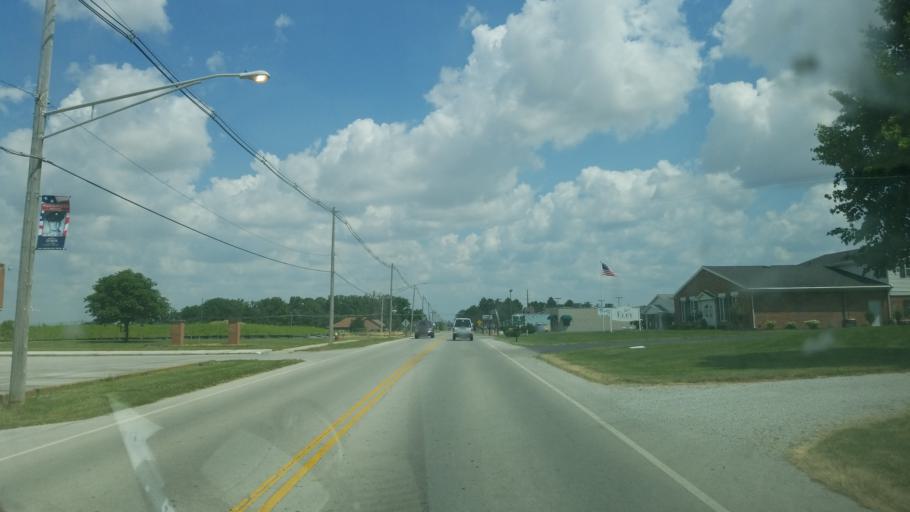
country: US
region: Ohio
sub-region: Auglaize County
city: Wapakoneta
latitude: 40.5815
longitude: -84.2028
